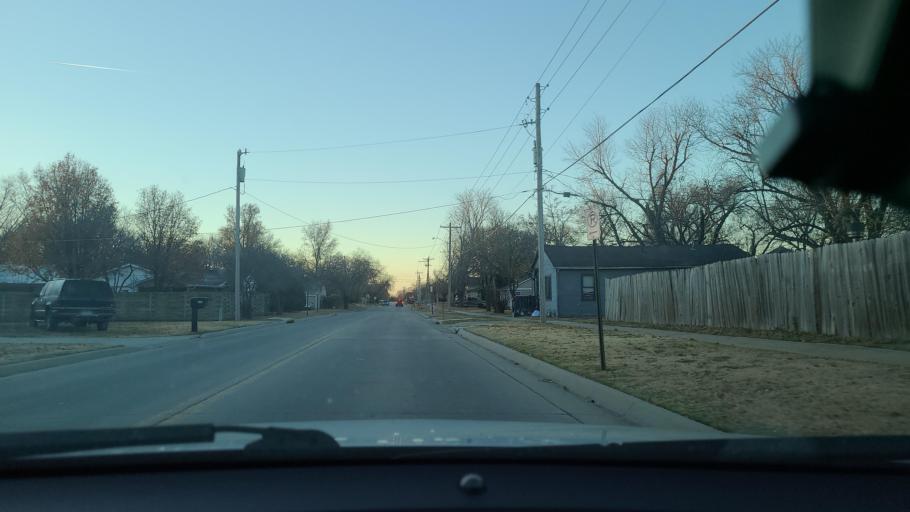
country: US
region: Kansas
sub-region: Sumner County
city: Wellington
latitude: 37.2678
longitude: -97.3852
